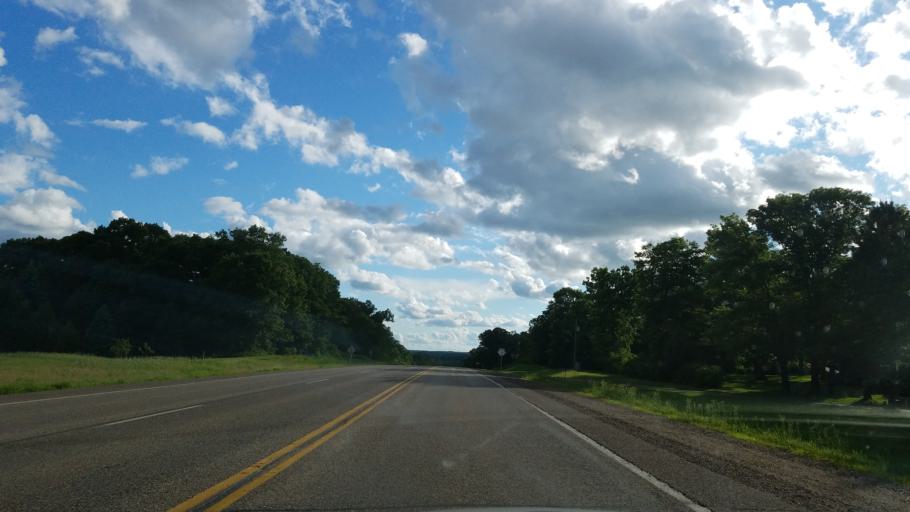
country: US
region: Wisconsin
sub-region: Polk County
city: Osceola
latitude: 45.3426
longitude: -92.6693
